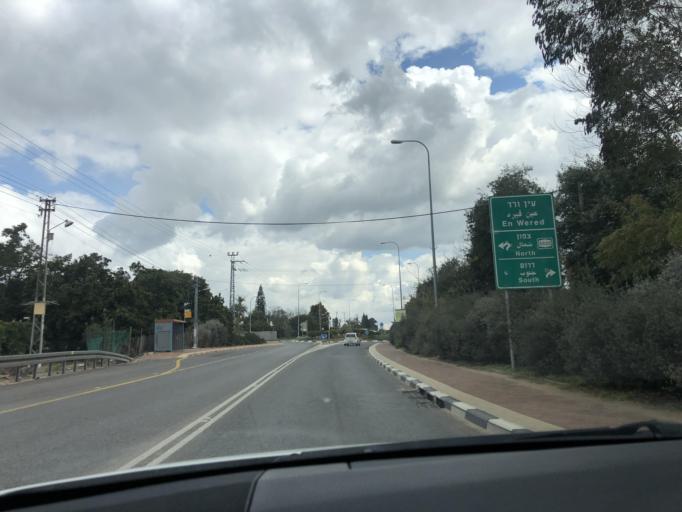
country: IL
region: Central District
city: Tel Mond
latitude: 32.2610
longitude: 34.9288
